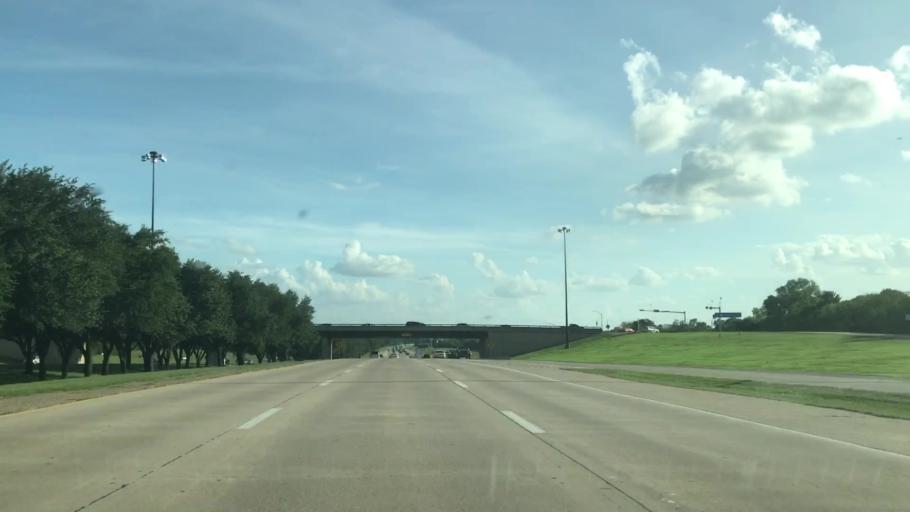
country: US
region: Texas
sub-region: Tarrant County
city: Euless
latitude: 32.8547
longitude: -97.0410
